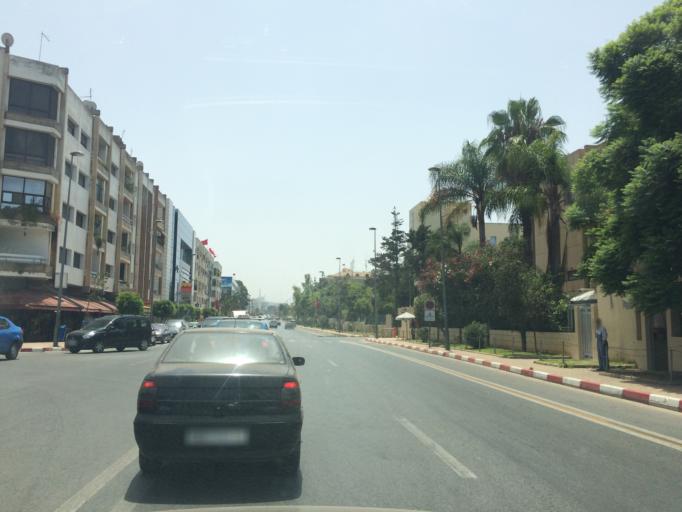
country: MA
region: Rabat-Sale-Zemmour-Zaer
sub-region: Rabat
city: Rabat
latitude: 33.9952
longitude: -6.8514
